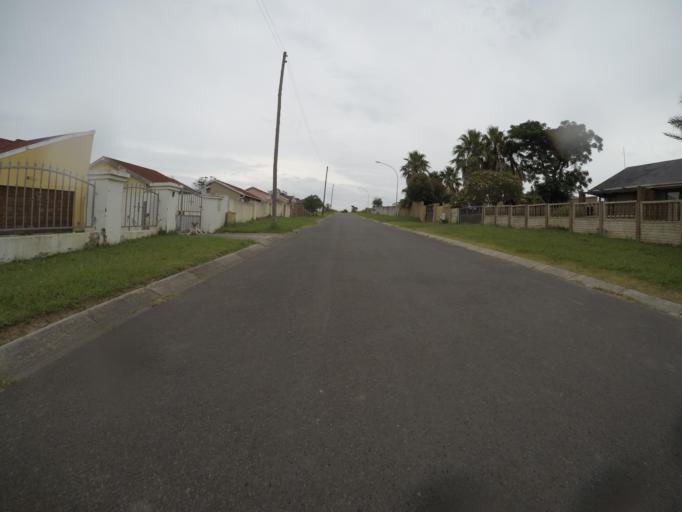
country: ZA
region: Eastern Cape
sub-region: Buffalo City Metropolitan Municipality
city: East London
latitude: -33.0010
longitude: 27.8513
